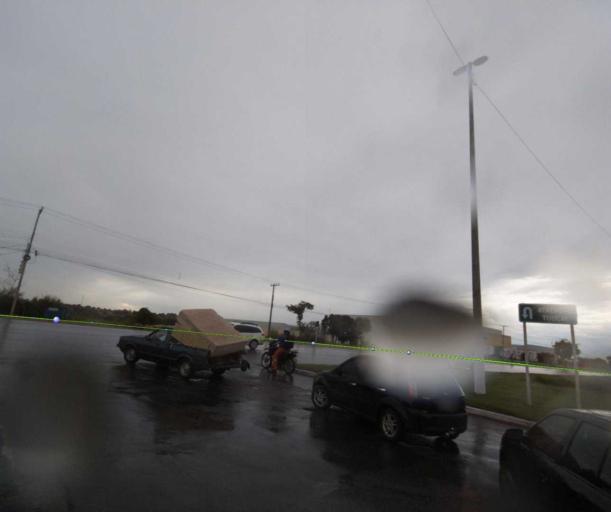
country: BR
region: Mato Grosso
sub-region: Cuiaba
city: Cuiaba
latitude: -15.6401
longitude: -56.0343
